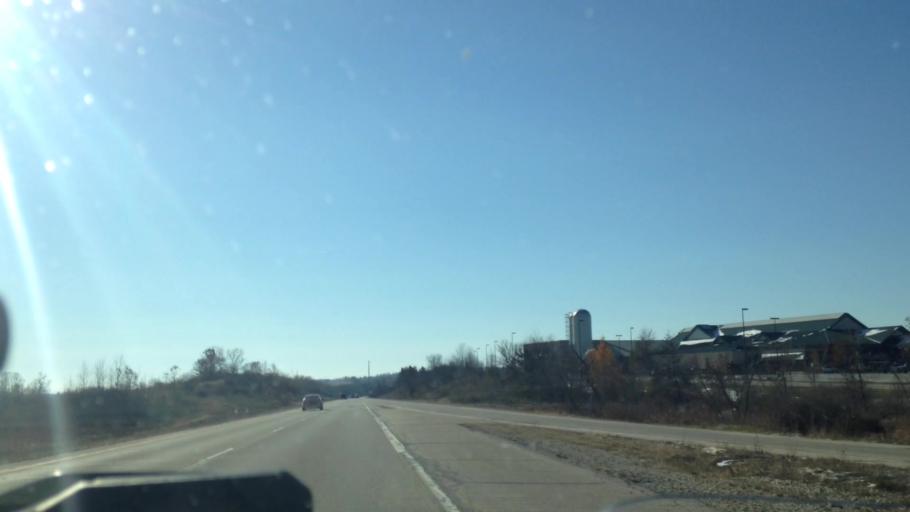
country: US
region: Wisconsin
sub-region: Washington County
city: Richfield
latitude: 43.2811
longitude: -88.1862
